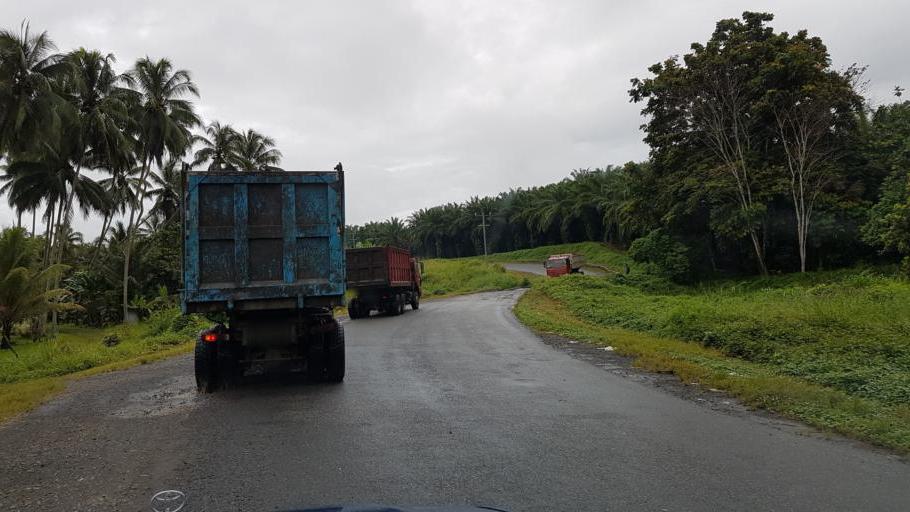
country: PG
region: Northern Province
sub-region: Sohe
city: Popondetta
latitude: -8.7647
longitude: 148.1780
